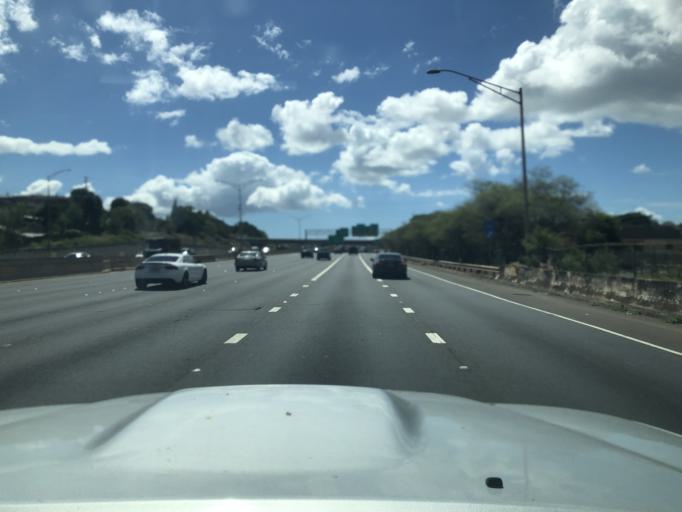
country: US
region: Hawaii
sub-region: Honolulu County
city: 'Aiea
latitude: 21.3795
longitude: -157.9290
